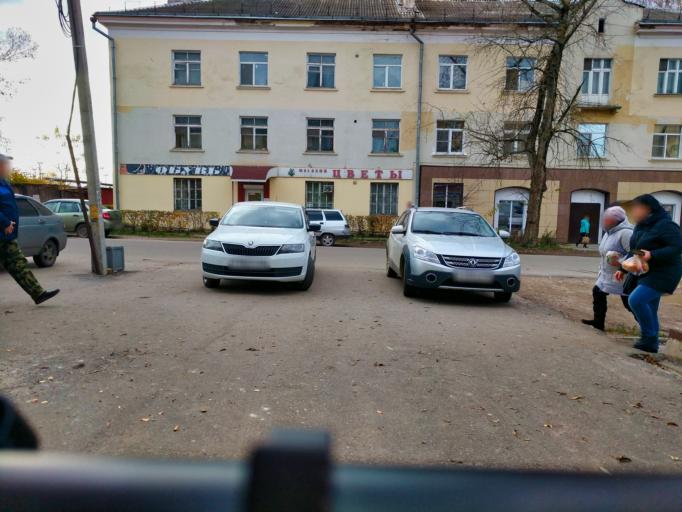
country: RU
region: Tverskaya
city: Rzhev
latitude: 56.2697
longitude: 34.3266
